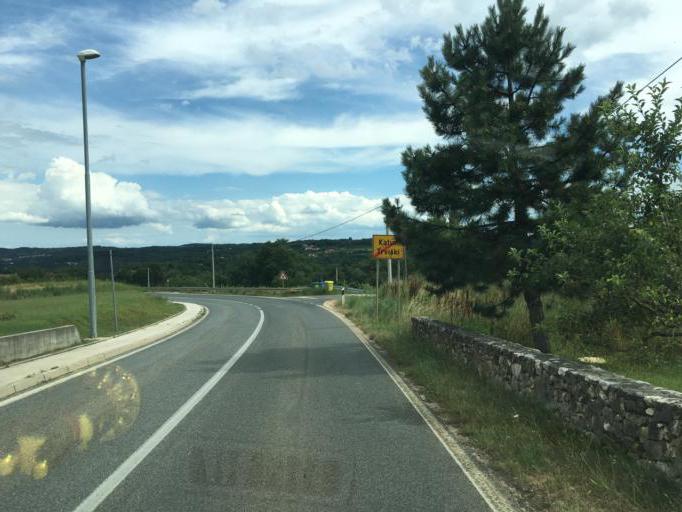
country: HR
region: Istarska
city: Pazin
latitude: 45.2548
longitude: 13.8743
